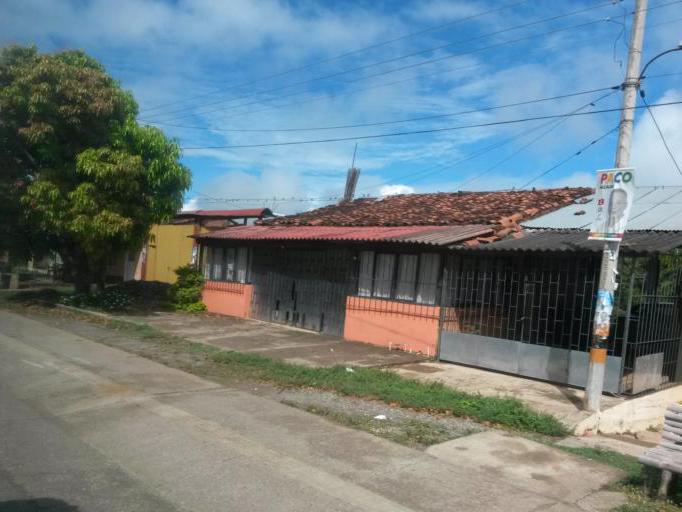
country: CO
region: Cauca
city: El Bordo
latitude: 2.1249
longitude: -76.9767
